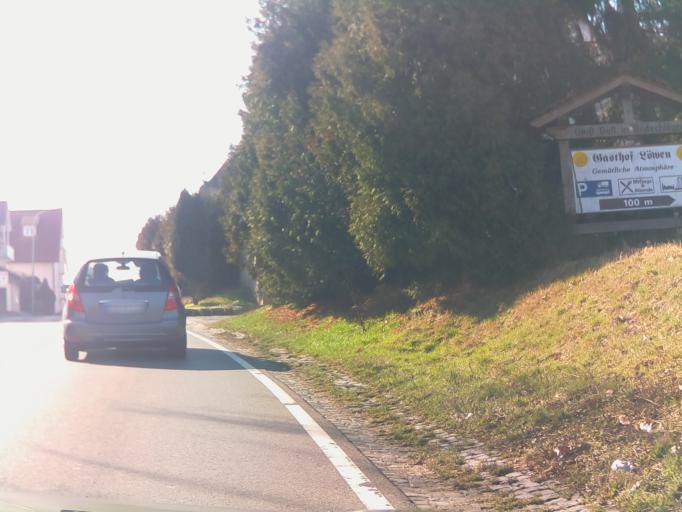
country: DE
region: Baden-Wuerttemberg
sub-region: Karlsruhe Region
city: Horb am Neckar
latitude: 48.4684
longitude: 8.7155
